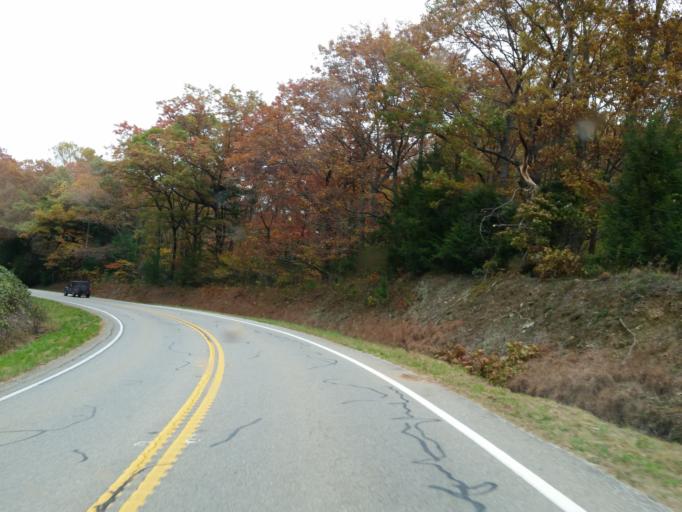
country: US
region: Georgia
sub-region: Pickens County
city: Jasper
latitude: 34.5336
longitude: -84.3770
